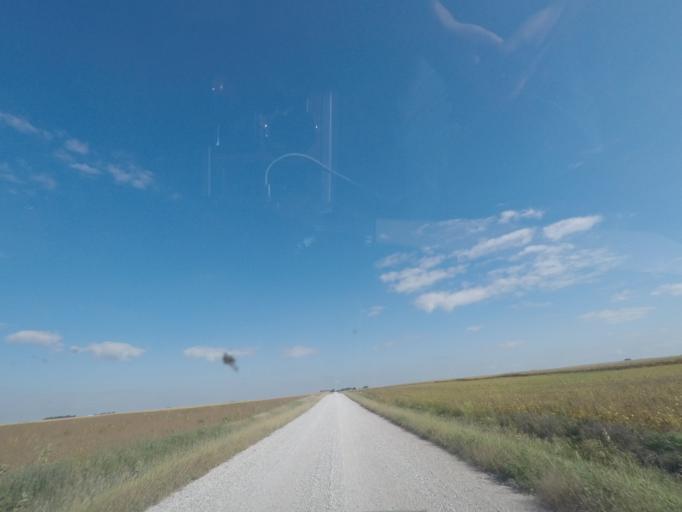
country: US
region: Iowa
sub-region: Story County
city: Nevada
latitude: 42.0456
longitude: -93.4252
